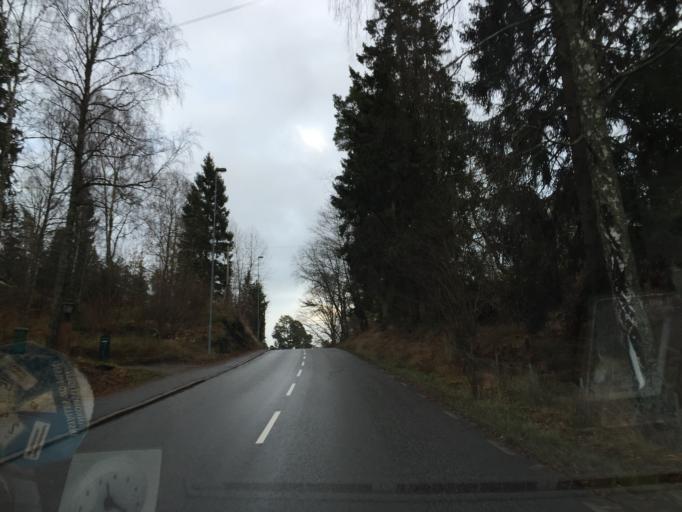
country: SE
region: Stockholm
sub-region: Salems Kommun
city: Ronninge
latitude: 59.1971
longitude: 17.7445
